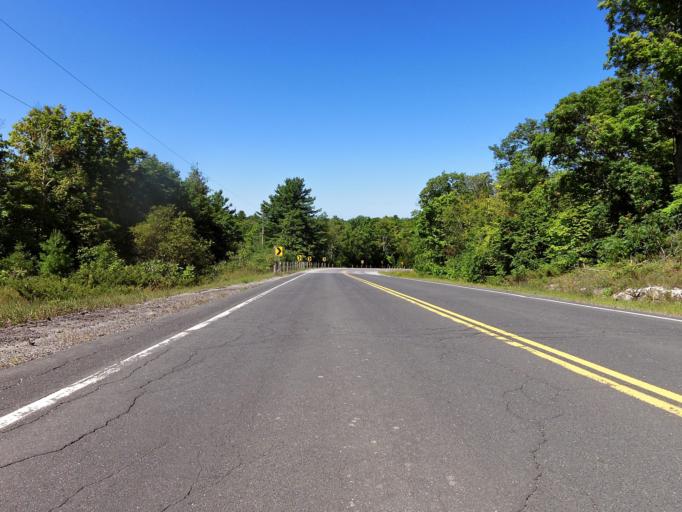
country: CA
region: Ontario
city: Arnprior
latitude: 45.1545
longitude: -76.5169
